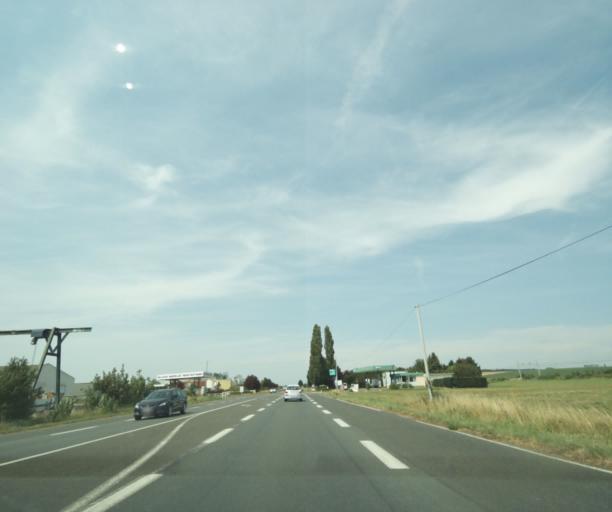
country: FR
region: Poitou-Charentes
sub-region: Departement de la Vienne
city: Dange-Saint-Romain
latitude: 46.9473
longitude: 0.6074
